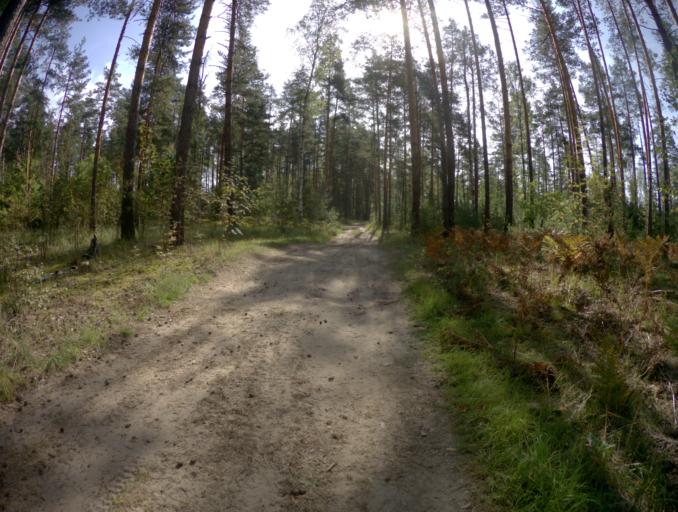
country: RU
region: Moskovskaya
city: Vereya
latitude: 55.8333
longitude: 39.0997
